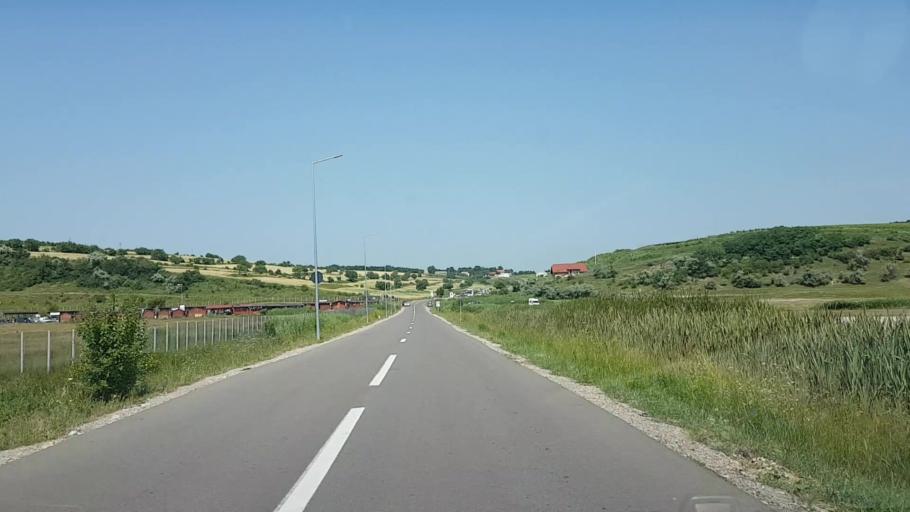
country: RO
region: Cluj
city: Turda
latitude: 46.5882
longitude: 23.7910
